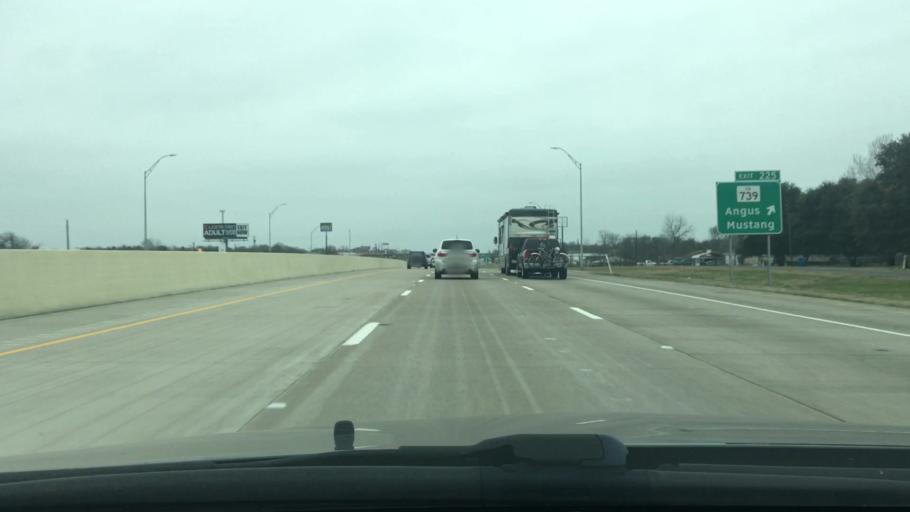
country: US
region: Texas
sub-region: Navarro County
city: Corsicana
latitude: 32.0135
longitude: -96.4362
